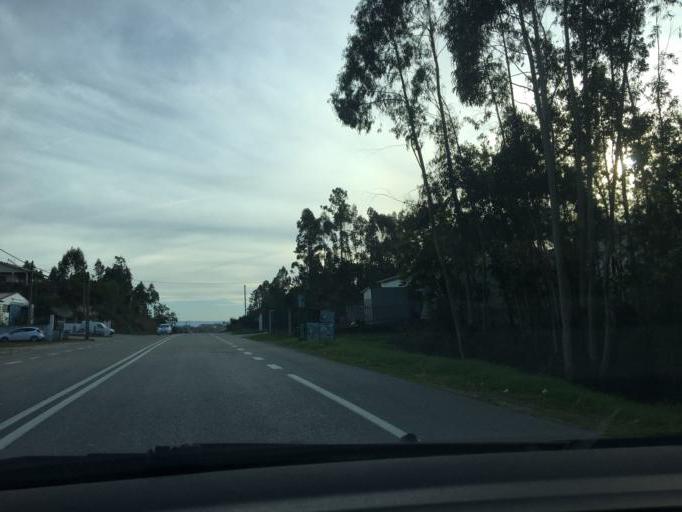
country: PT
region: Coimbra
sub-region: Montemor-O-Velho
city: Arazede
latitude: 40.2182
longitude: -8.5953
